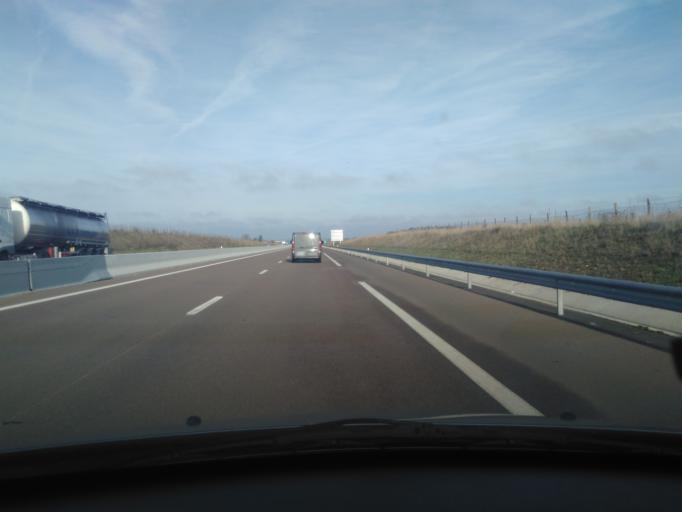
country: FR
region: Bourgogne
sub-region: Departement de la Nievre
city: Saint-Pierre-le-Moutier
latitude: 46.8071
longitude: 3.1212
